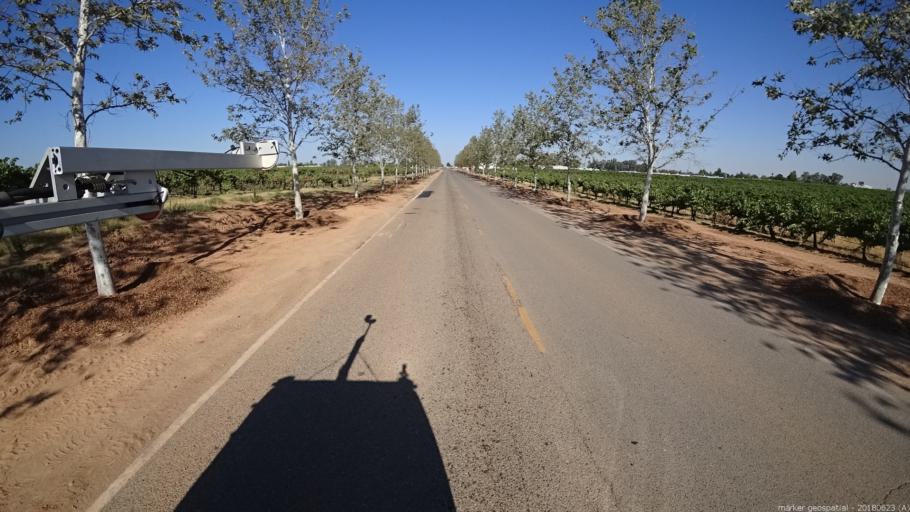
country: US
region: California
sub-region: Madera County
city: Bonadelle Ranchos-Madera Ranchos
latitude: 36.9595
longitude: -119.7903
